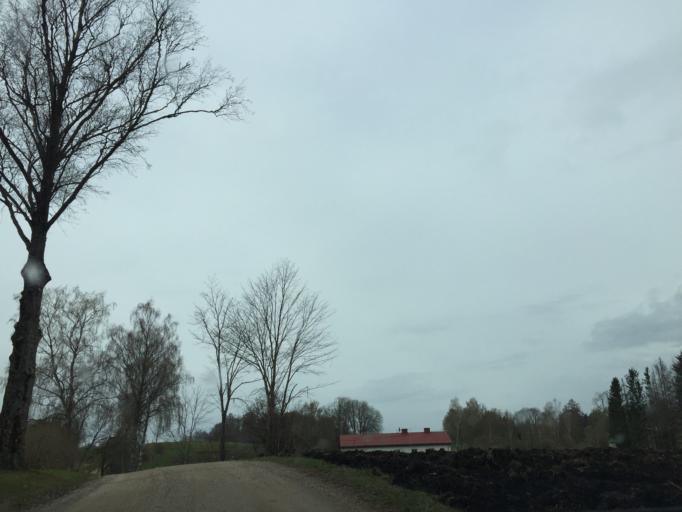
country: LV
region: Amatas Novads
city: Drabesi
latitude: 57.2536
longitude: 25.2796
